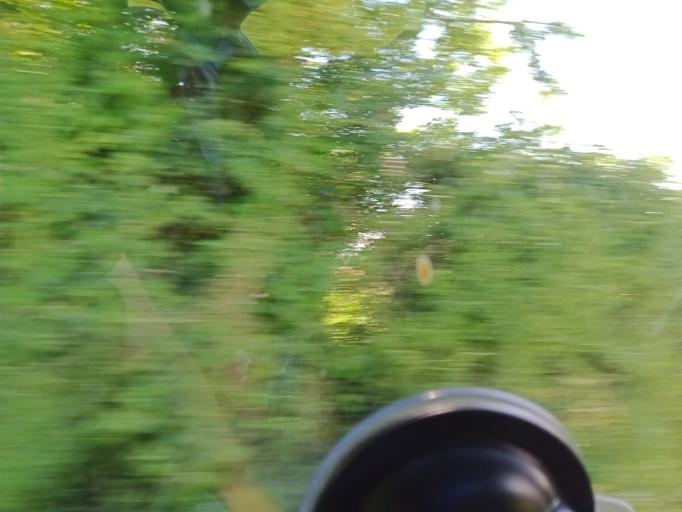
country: IE
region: Leinster
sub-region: Kilkenny
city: Thomastown
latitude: 52.5556
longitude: -7.1042
